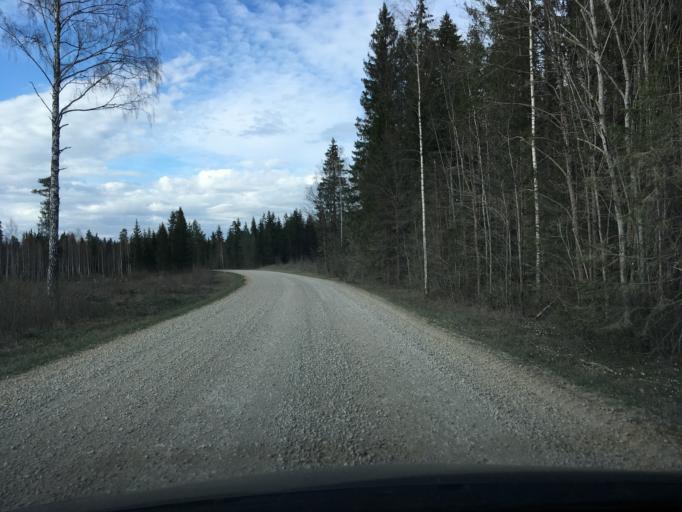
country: EE
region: Raplamaa
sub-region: Maerjamaa vald
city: Marjamaa
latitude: 58.9605
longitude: 24.3292
